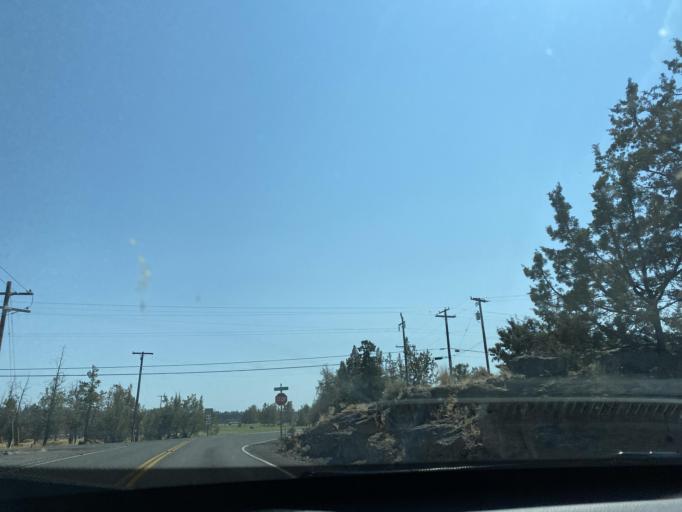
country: US
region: Oregon
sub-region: Deschutes County
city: Terrebonne
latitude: 44.3567
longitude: -121.1587
